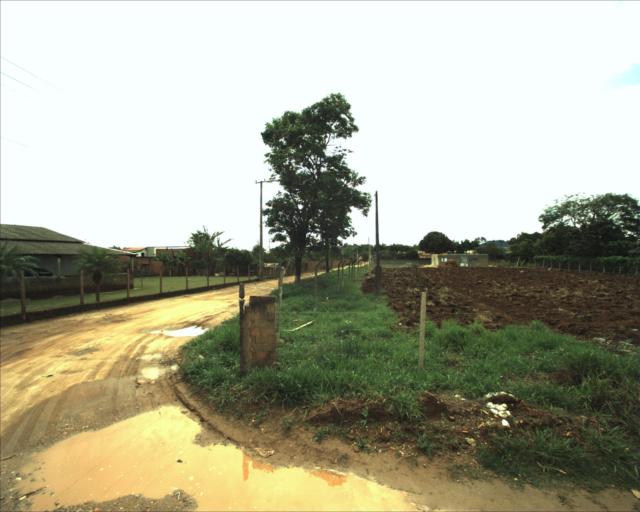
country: BR
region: Sao Paulo
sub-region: Aracoiaba Da Serra
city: Aracoiaba da Serra
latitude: -23.5602
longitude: -47.5564
